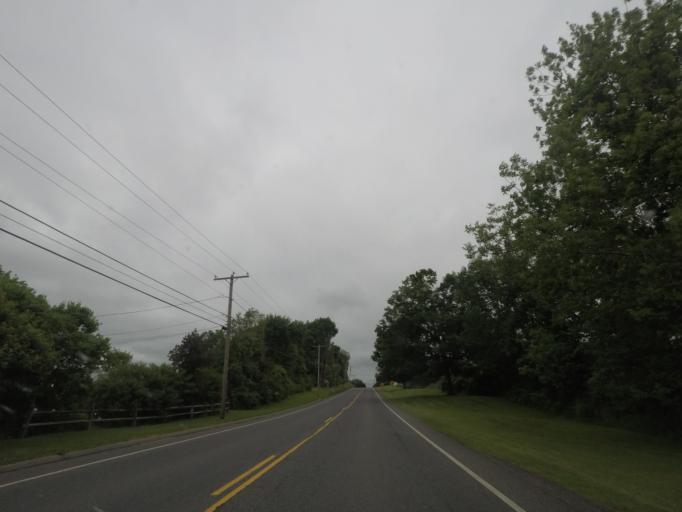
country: US
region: Connecticut
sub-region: Litchfield County
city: Canaan
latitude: 41.9355
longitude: -73.4291
